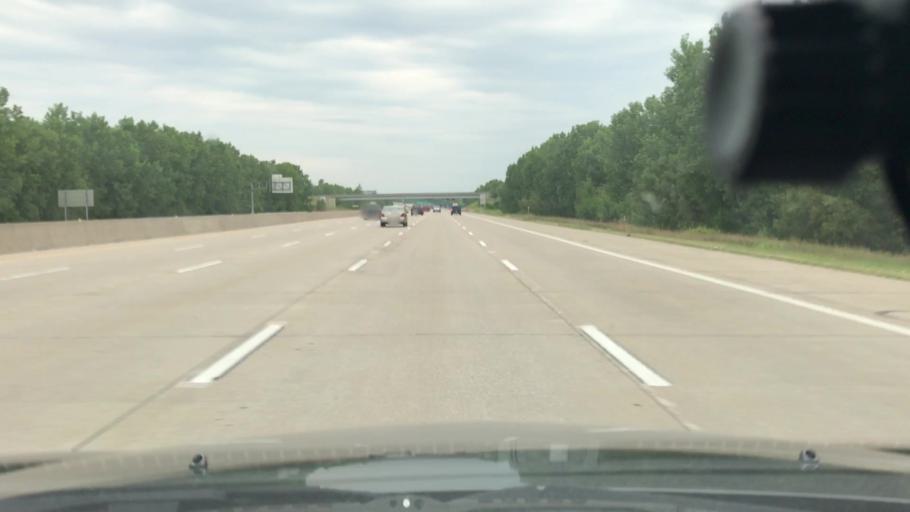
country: US
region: Missouri
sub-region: Saint Charles County
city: Saint Charles
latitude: 38.7156
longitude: -90.5084
